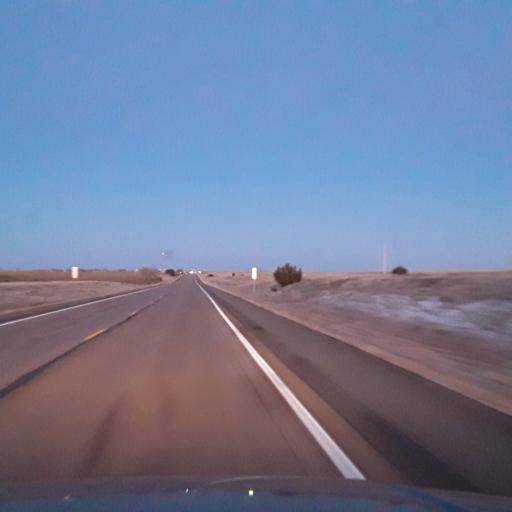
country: US
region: New Mexico
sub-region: Guadalupe County
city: Santa Rosa
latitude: 34.7718
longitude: -104.9633
